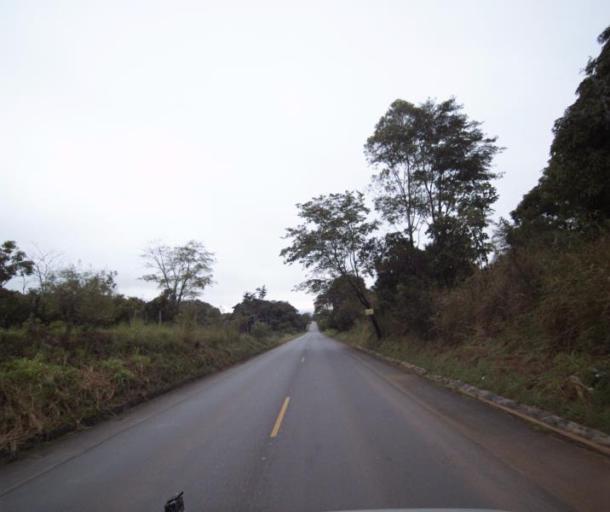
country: BR
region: Goias
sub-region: Pirenopolis
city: Pirenopolis
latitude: -15.8807
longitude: -48.7904
